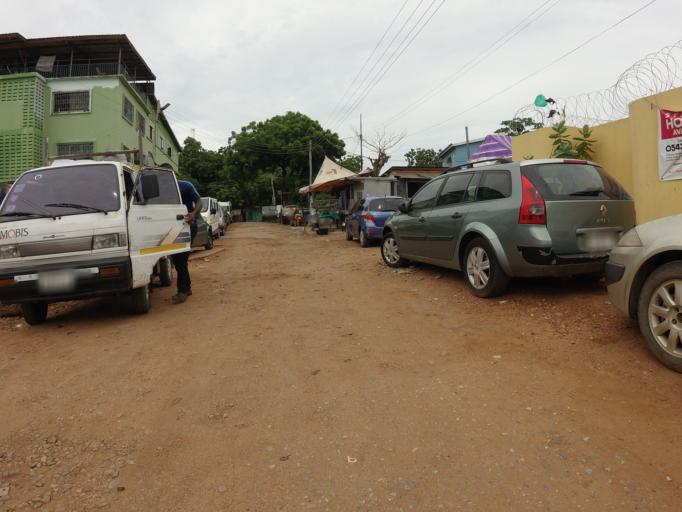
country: GH
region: Greater Accra
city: Accra
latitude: 5.5977
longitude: -0.2239
